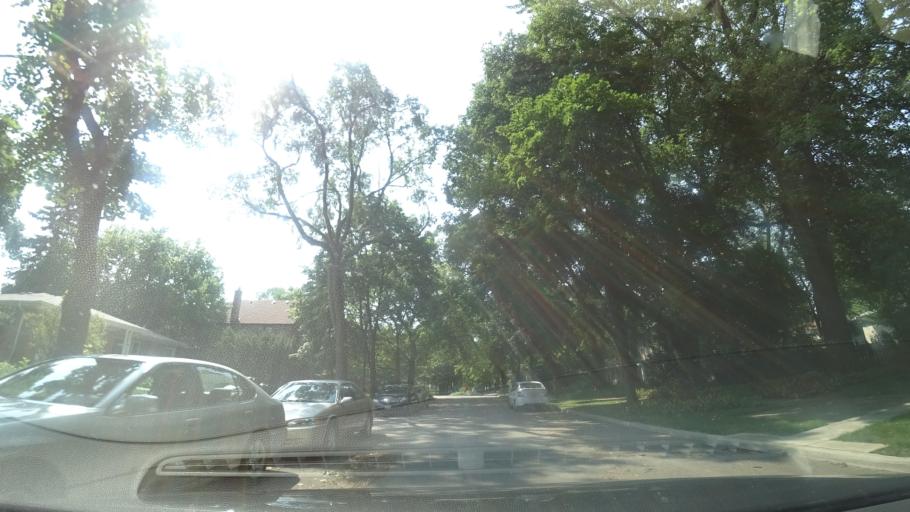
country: US
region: Illinois
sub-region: Cook County
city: Evanston
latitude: 42.0256
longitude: -87.6948
